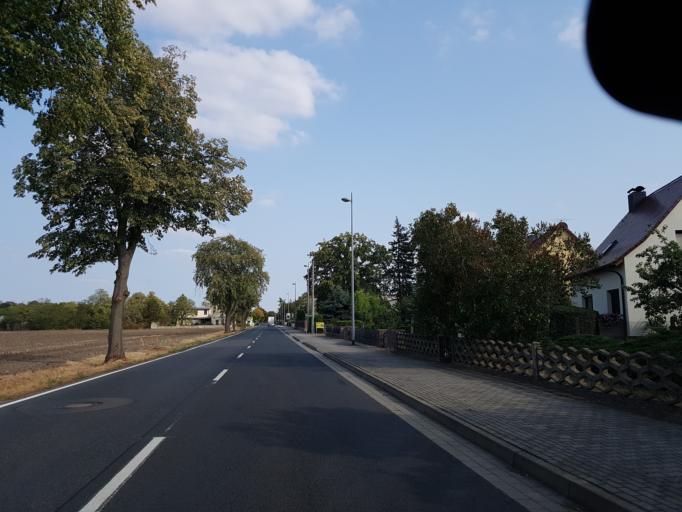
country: DE
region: Saxony-Anhalt
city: Pretzsch
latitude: 51.7198
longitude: 12.7967
